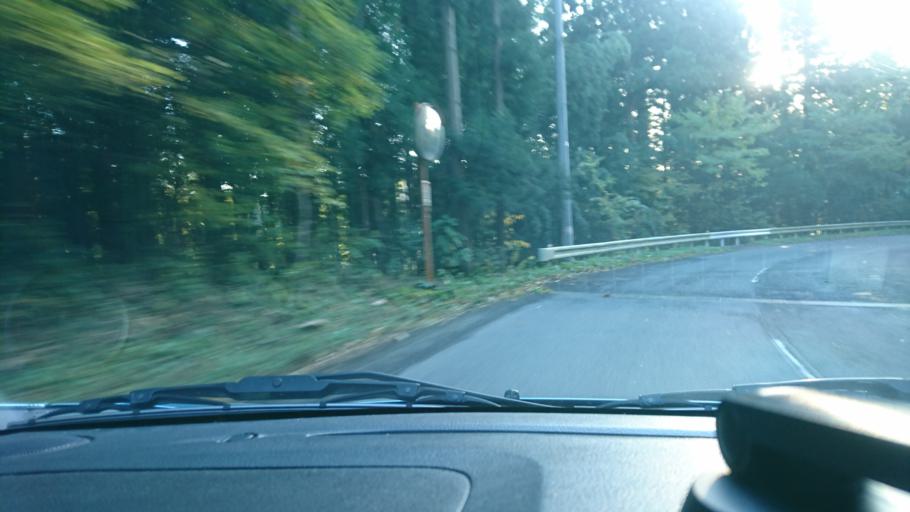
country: JP
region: Iwate
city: Ichinoseki
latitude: 38.7946
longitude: 141.2525
